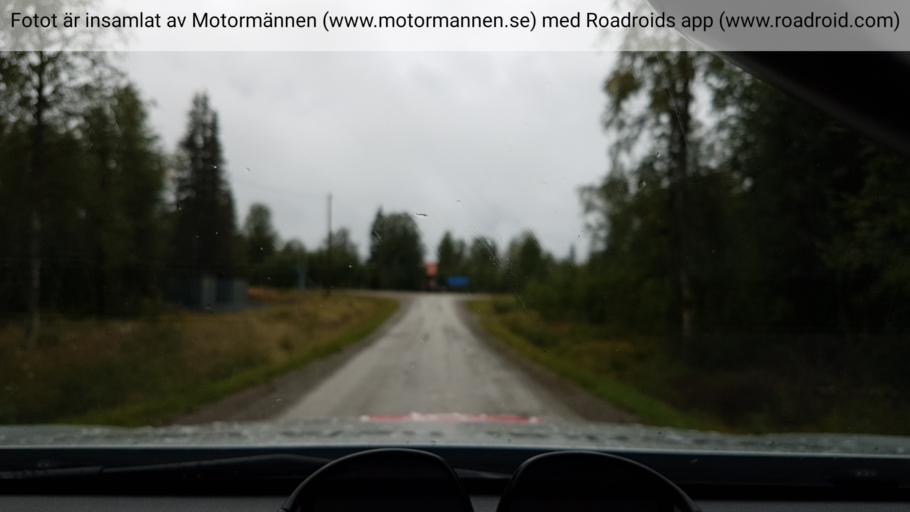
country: SE
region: Vaesterbotten
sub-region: Storumans Kommun
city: Storuman
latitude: 64.9295
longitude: 17.2481
